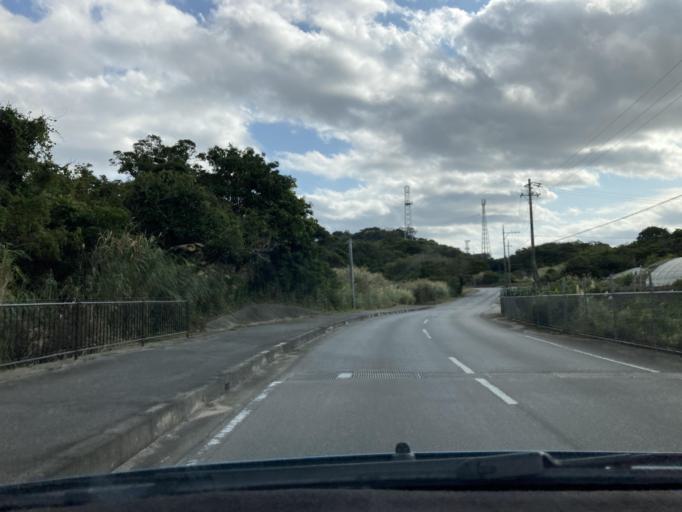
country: JP
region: Okinawa
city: Tomigusuku
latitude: 26.1764
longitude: 127.7613
